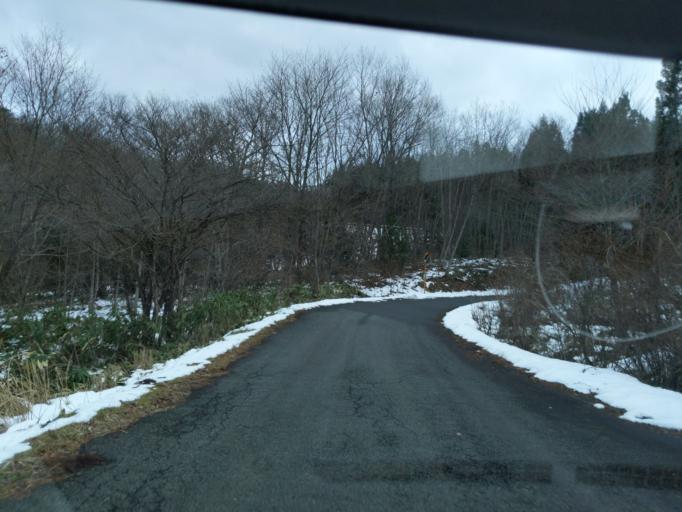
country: JP
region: Iwate
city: Ichinoseki
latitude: 38.9957
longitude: 140.9984
